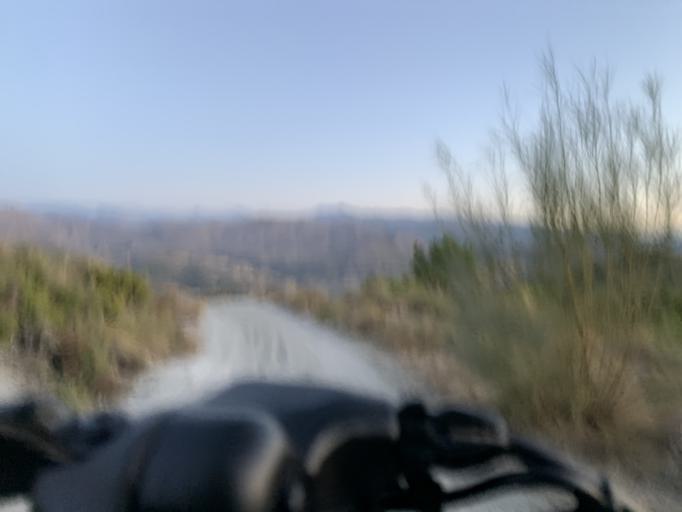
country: ES
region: Andalusia
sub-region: Provincia de Granada
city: Beas de Granada
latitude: 37.2219
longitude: -3.4560
